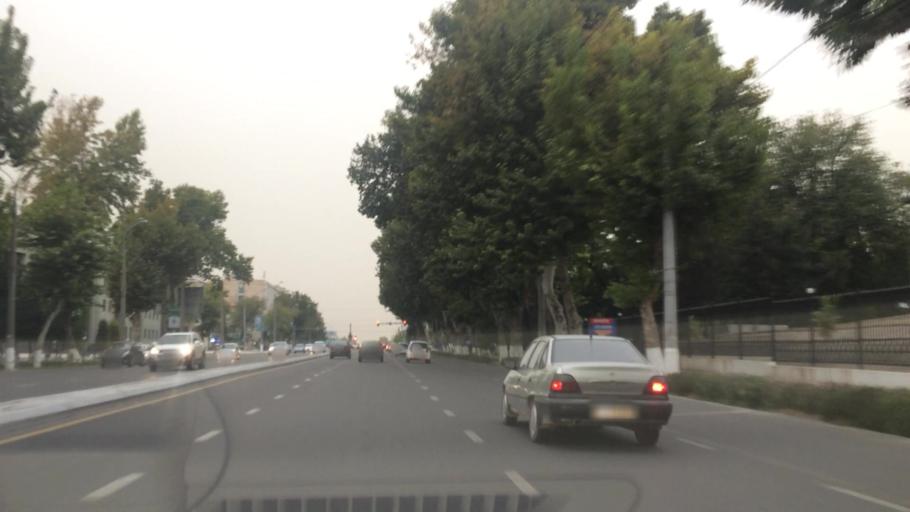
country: UZ
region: Toshkent Shahri
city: Tashkent
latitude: 41.3025
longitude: 69.2785
